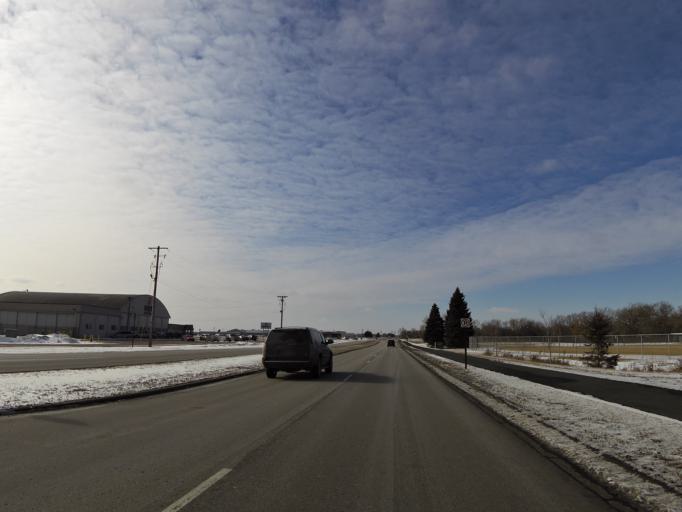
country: US
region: Minnesota
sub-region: Hennepin County
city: Eden Prairie
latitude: 44.8298
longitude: -93.4498
